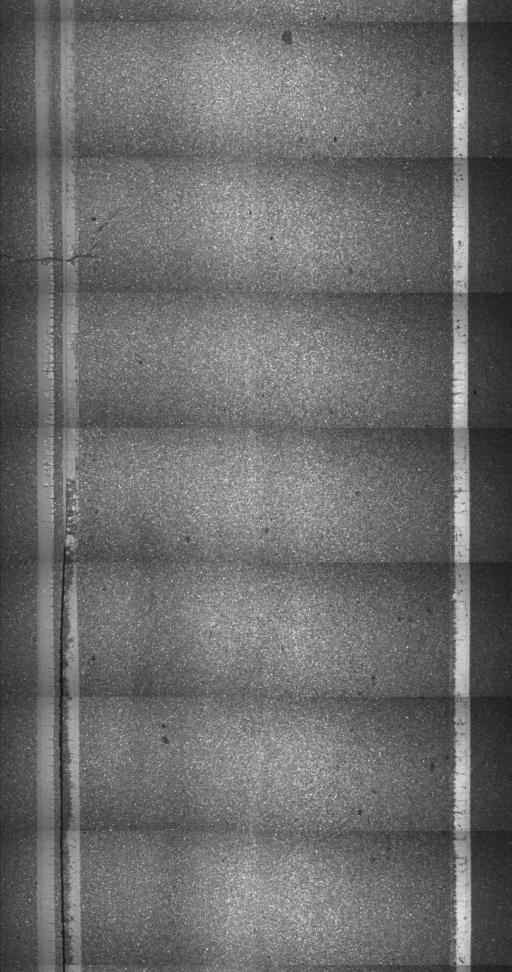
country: US
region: Vermont
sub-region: Orange County
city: Randolph
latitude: 43.9435
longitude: -72.8410
